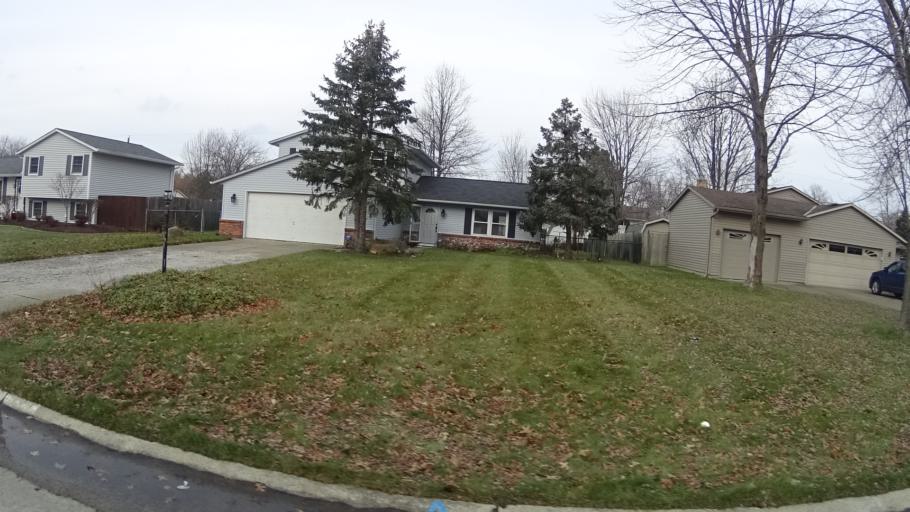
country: US
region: Ohio
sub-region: Lorain County
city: Amherst
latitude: 41.4031
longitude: -82.1872
